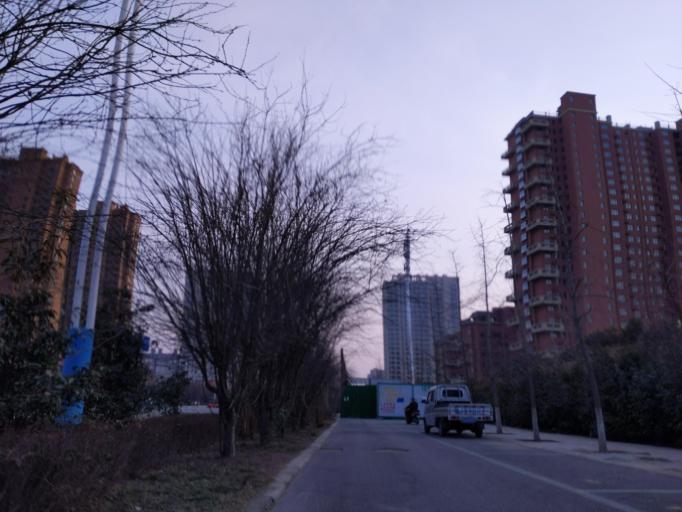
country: CN
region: Henan Sheng
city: Zhongyuanlu
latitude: 35.7832
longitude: 115.1271
